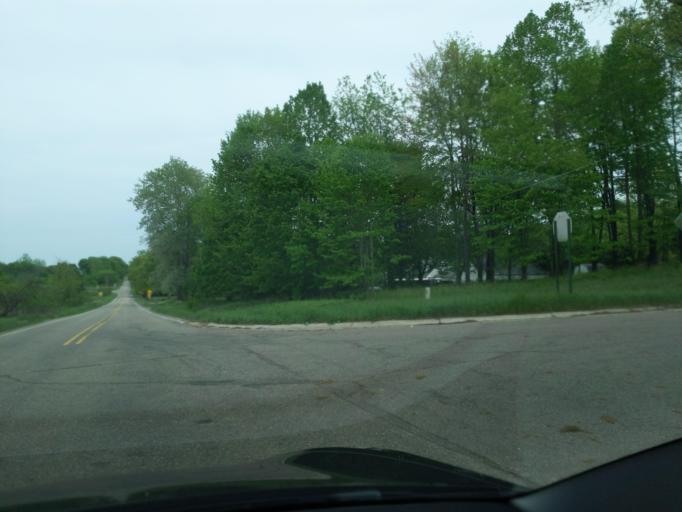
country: US
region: Michigan
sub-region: Ingham County
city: Leslie
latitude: 42.4657
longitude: -84.4280
